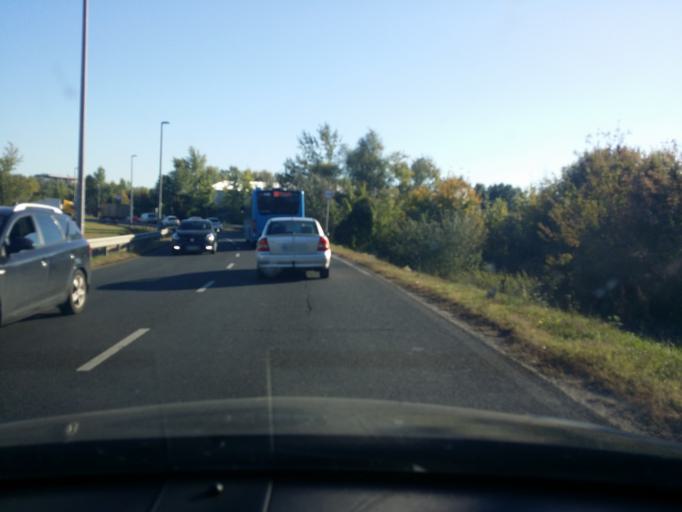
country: HU
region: Pest
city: Dunakeszi
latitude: 47.6068
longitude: 19.1104
